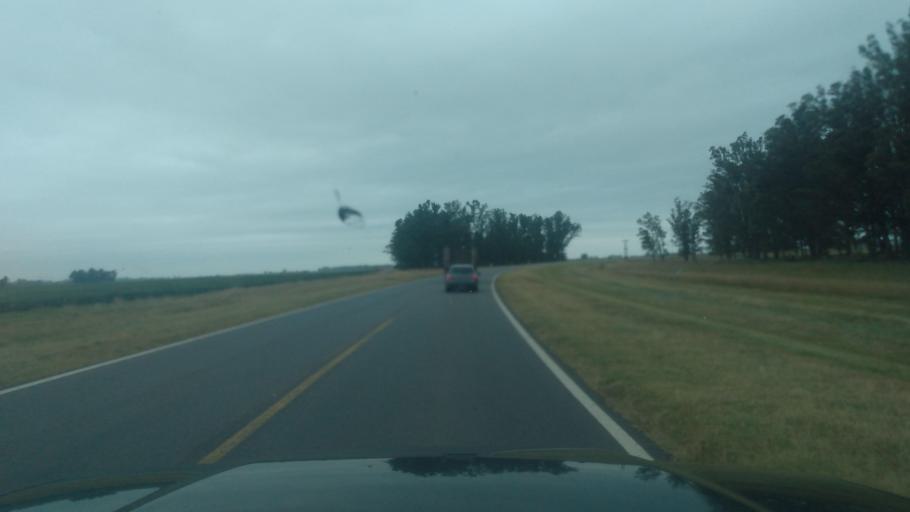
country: AR
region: Buenos Aires
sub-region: Partido de Nueve de Julio
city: Nueve de Julio
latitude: -35.4015
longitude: -60.7658
